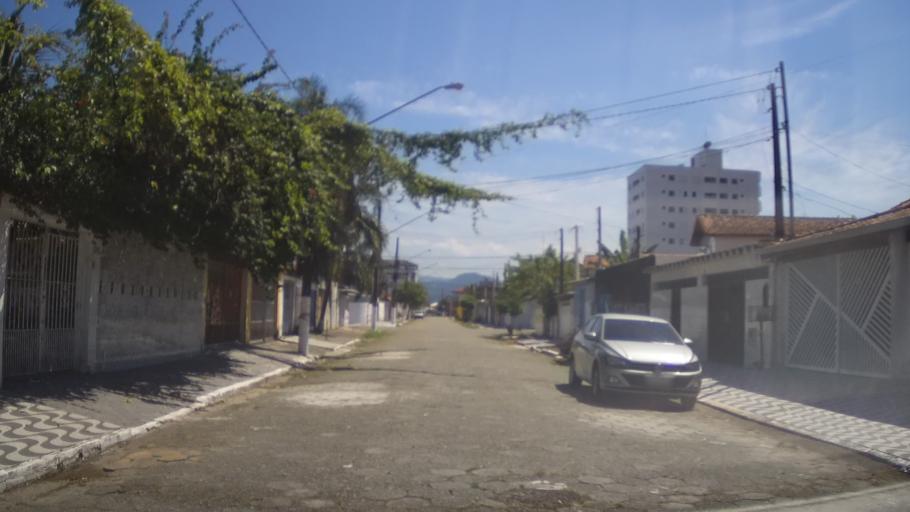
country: BR
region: Sao Paulo
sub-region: Praia Grande
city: Praia Grande
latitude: -24.0115
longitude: -46.4349
